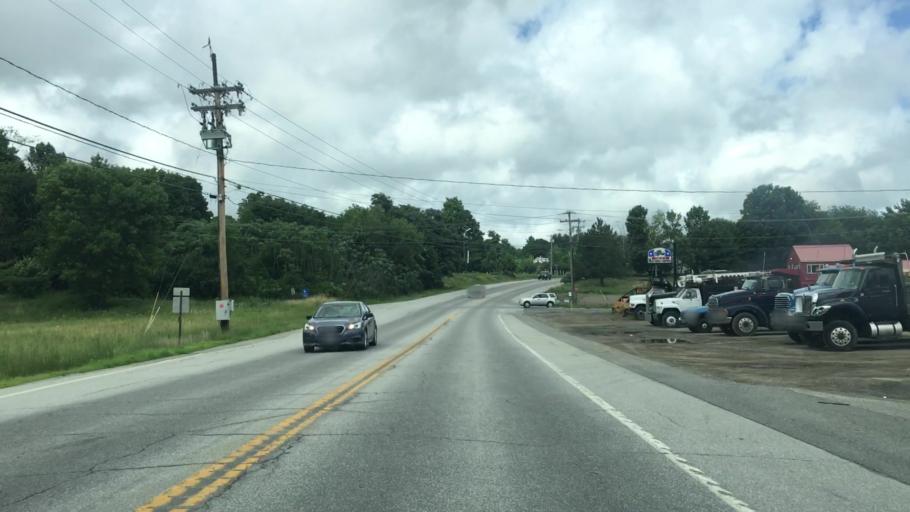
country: US
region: Maine
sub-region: Kennebec County
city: Hallowell
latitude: 44.2845
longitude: -69.7769
